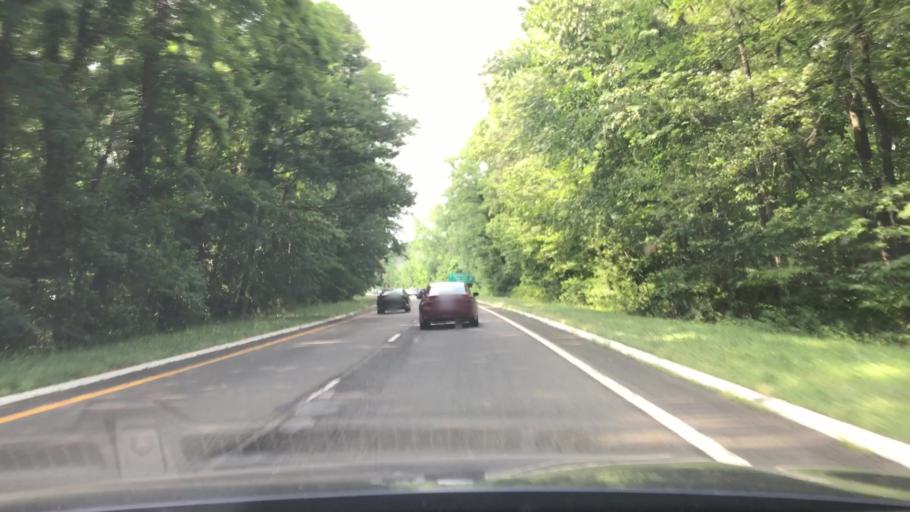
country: US
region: New York
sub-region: Rockland County
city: Bardonia
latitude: 41.1161
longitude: -74.0028
